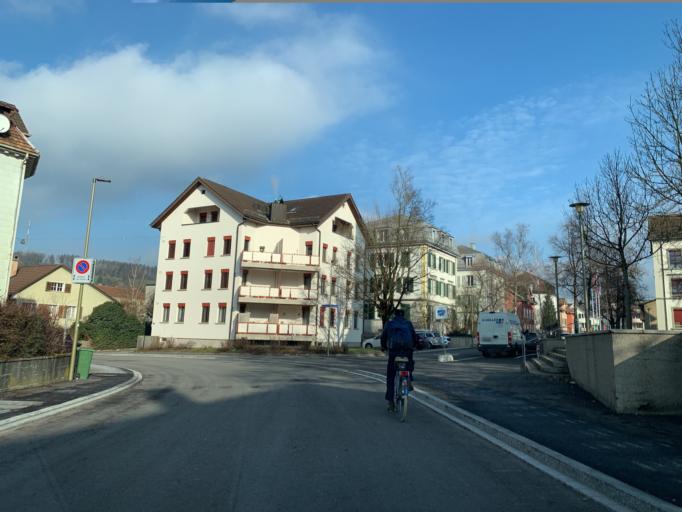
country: CH
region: Zurich
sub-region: Bezirk Winterthur
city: Toess (Kreis 4) / Eichliacker
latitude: 47.4904
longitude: 8.7080
